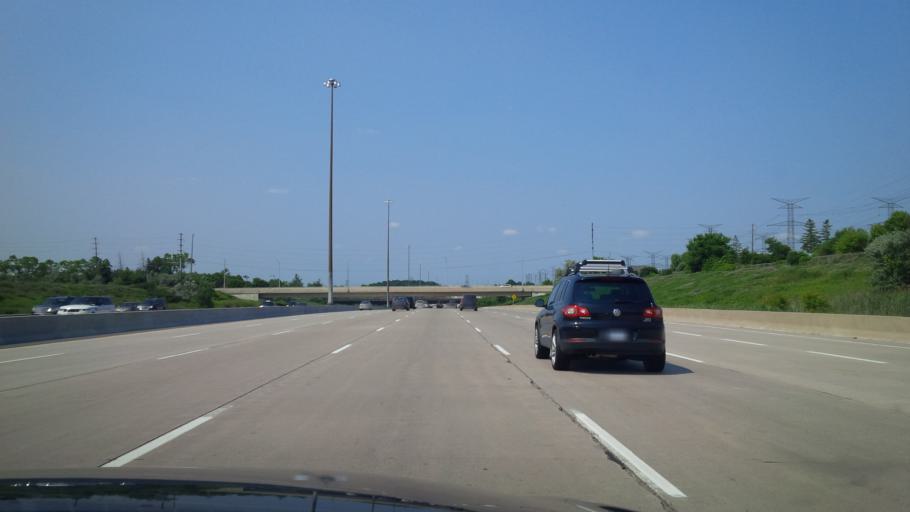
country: CA
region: Ontario
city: Concord
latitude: 43.7721
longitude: -79.5756
